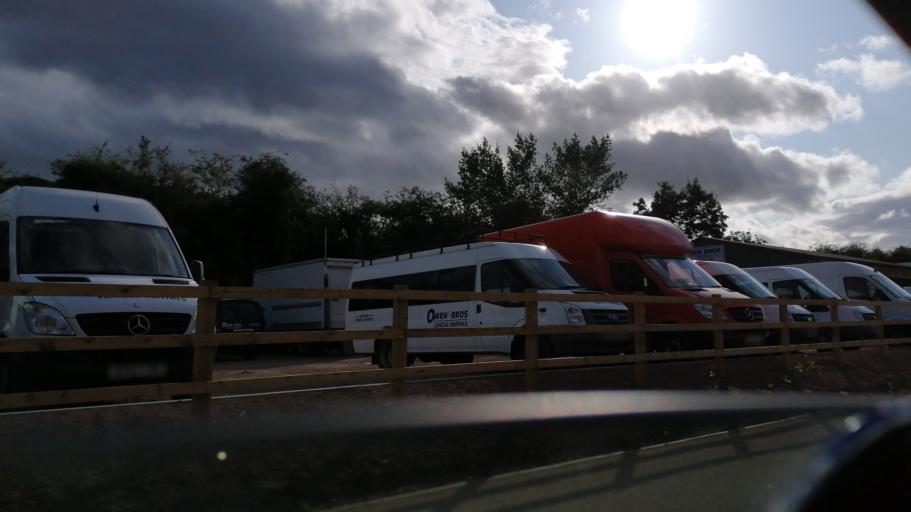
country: GB
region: England
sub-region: Herefordshire
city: Lower Bullingham
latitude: 52.0378
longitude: -2.6839
